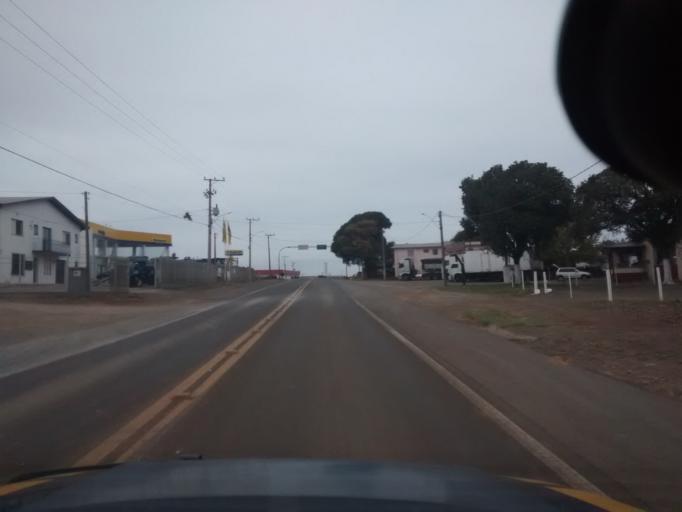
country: BR
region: Rio Grande do Sul
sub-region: Vacaria
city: Vacaria
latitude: -28.4809
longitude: -50.9630
